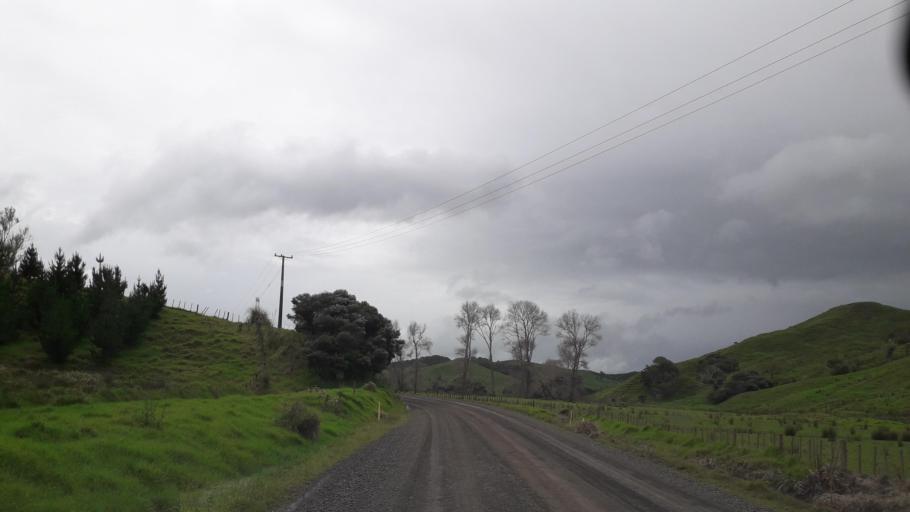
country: NZ
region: Northland
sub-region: Far North District
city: Ahipara
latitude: -35.4267
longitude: 173.3560
